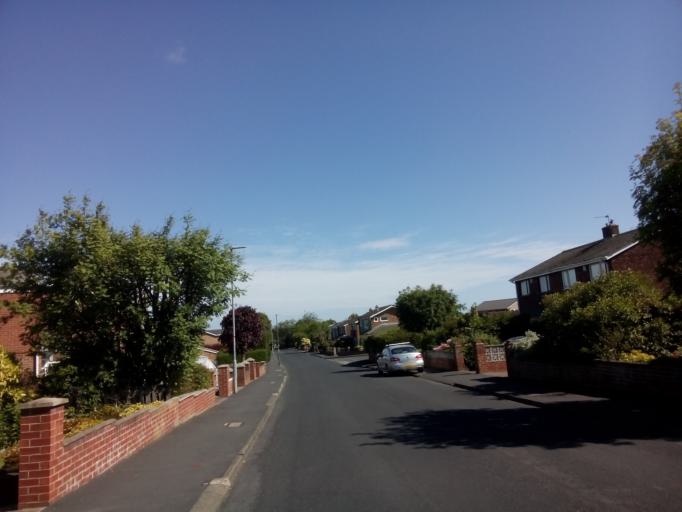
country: GB
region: England
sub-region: County Durham
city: Durham
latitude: 54.7844
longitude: -1.5463
